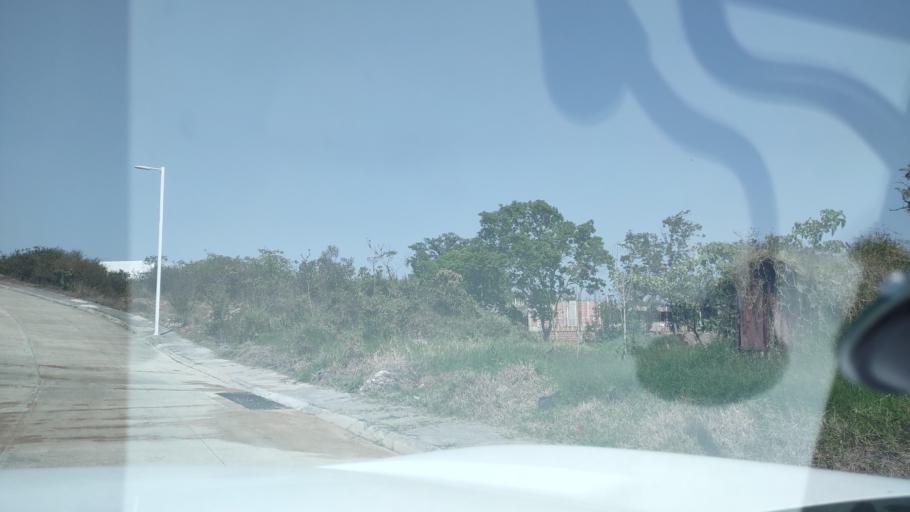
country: MX
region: Veracruz
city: El Castillo
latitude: 19.5291
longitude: -96.8679
